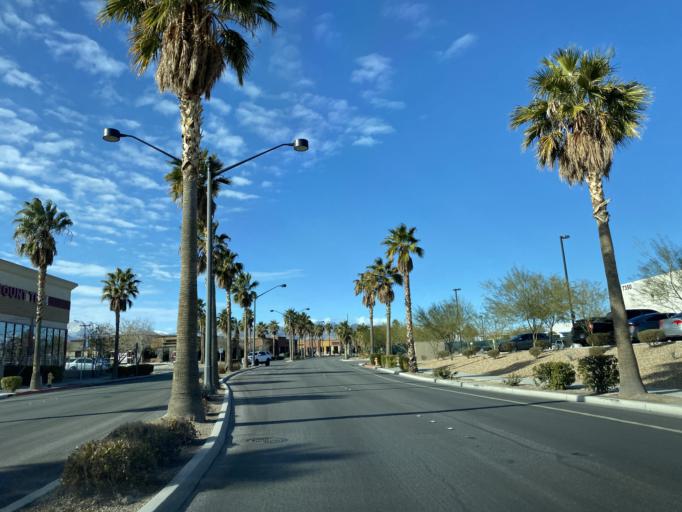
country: US
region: Nevada
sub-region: Clark County
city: Las Vegas
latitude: 36.2738
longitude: -115.2550
